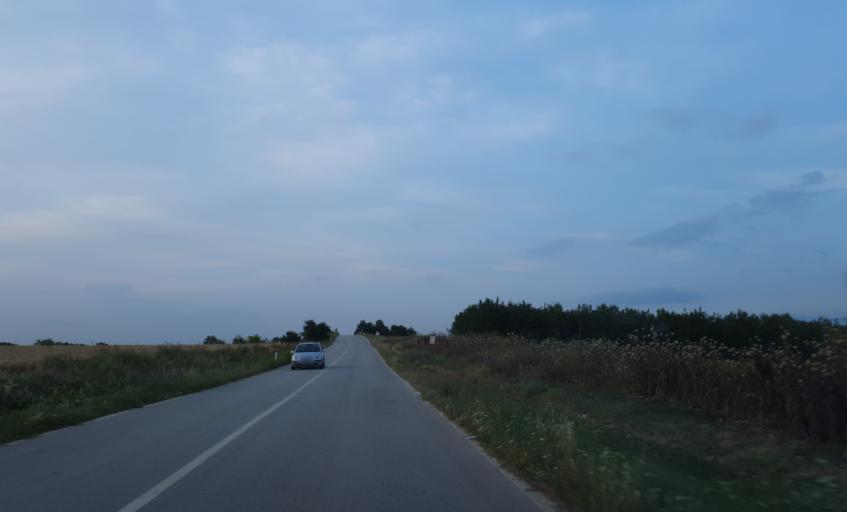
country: TR
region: Kirklareli
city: Buyukkaristiran
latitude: 41.3627
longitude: 27.6061
